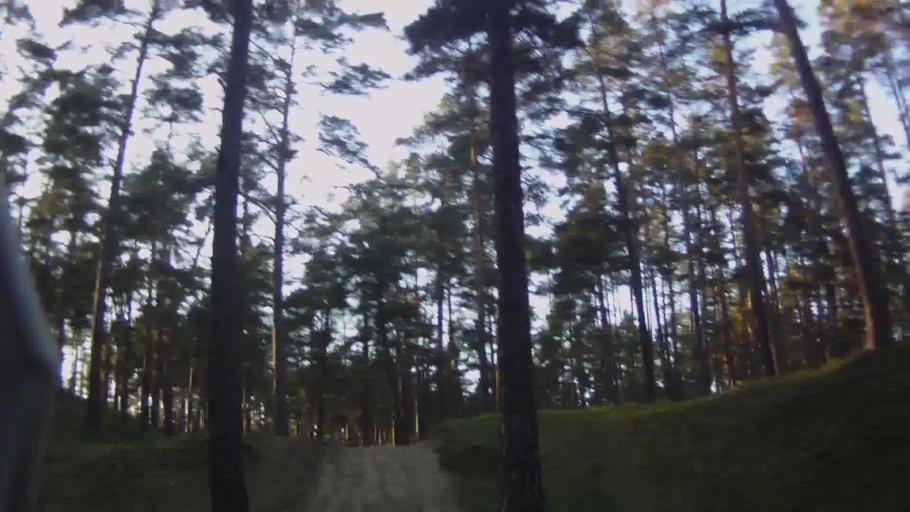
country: LV
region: Riga
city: Jaunciems
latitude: 57.0618
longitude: 24.1783
